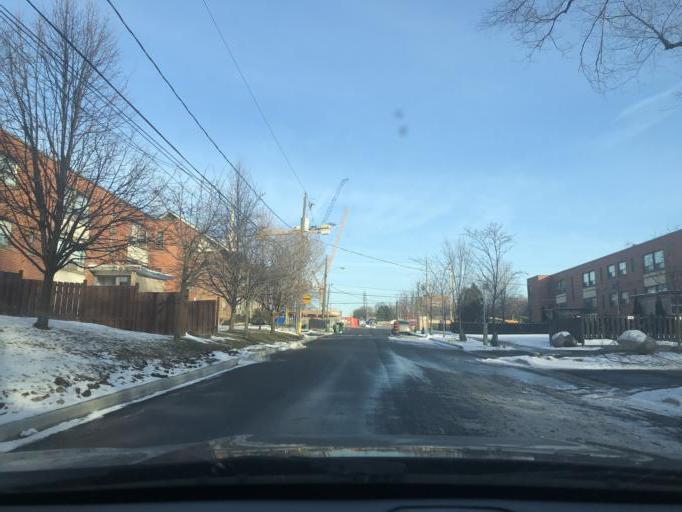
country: CA
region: Ontario
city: Toronto
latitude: 43.6970
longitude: -79.4769
